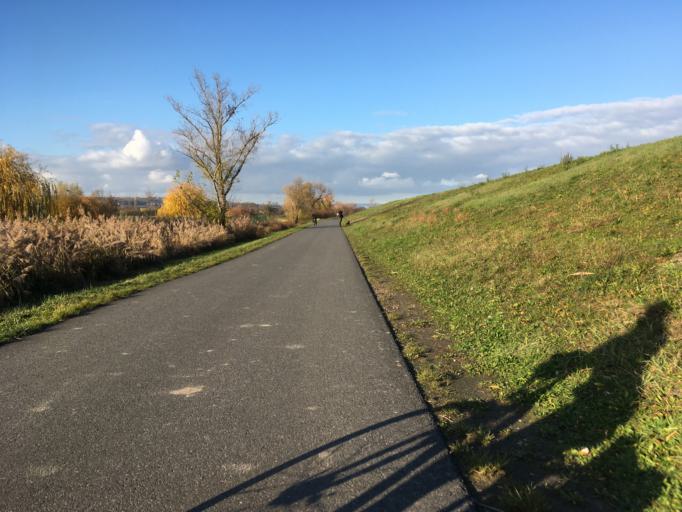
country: DE
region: Rheinland-Pfalz
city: Bodenheim
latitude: 49.9309
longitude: 8.3311
